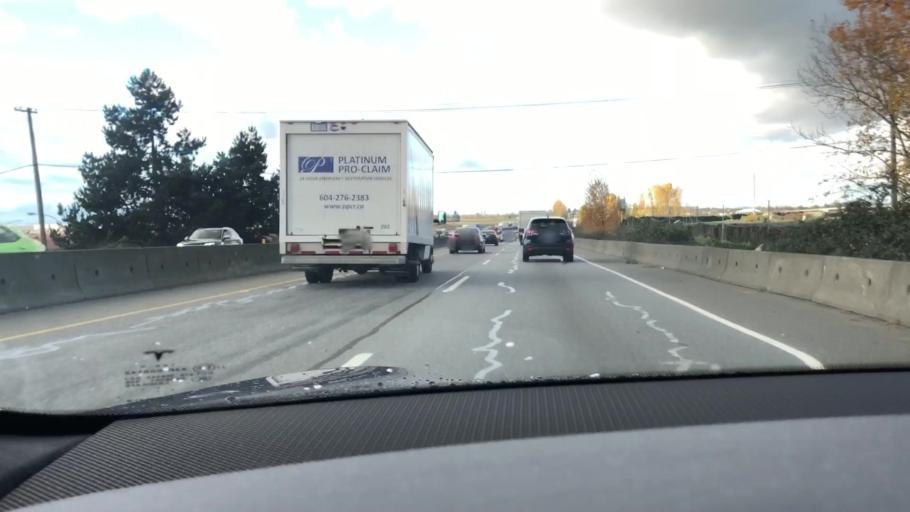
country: CA
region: British Columbia
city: New Westminster
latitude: 49.1697
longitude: -123.0015
